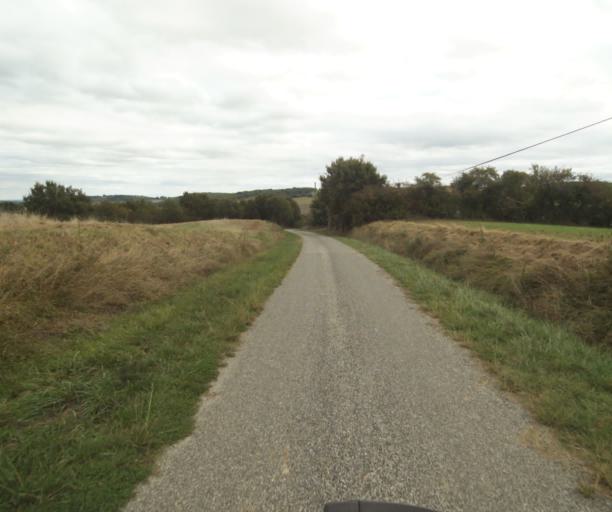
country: FR
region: Midi-Pyrenees
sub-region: Departement du Tarn-et-Garonne
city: Beaumont-de-Lomagne
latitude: 43.8525
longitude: 1.0778
